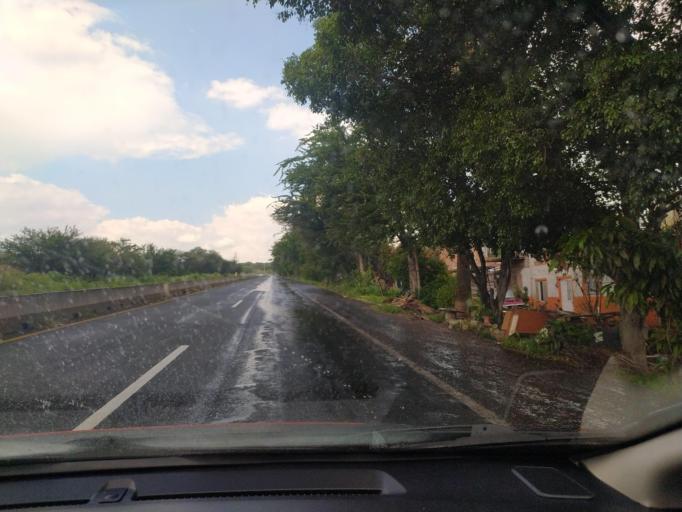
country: MX
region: Jalisco
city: Bellavista
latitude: 20.4298
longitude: -103.6023
